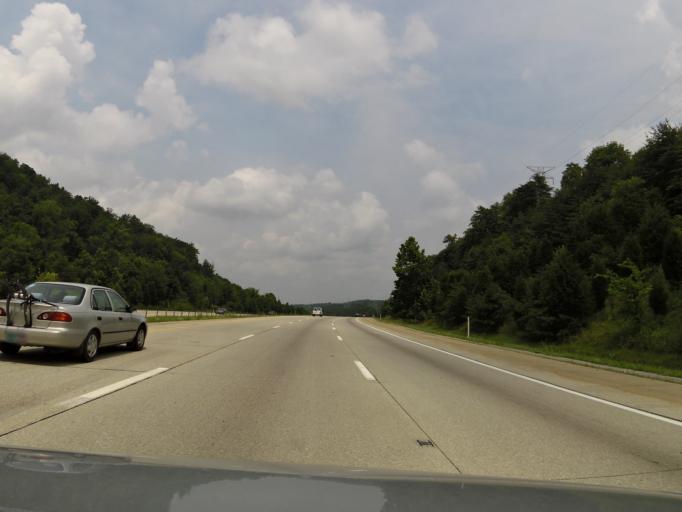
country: US
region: Kentucky
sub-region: Bullitt County
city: Lebanon Junction
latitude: 37.8801
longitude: -85.7019
